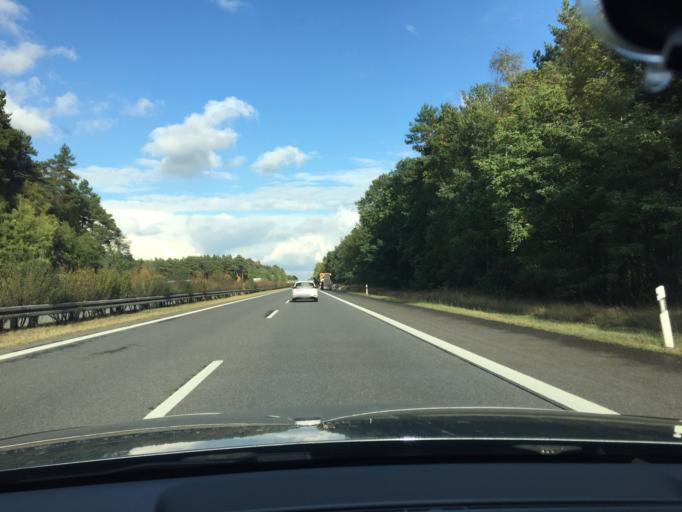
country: DE
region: Brandenburg
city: Lubbenau
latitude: 51.8131
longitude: 13.8915
